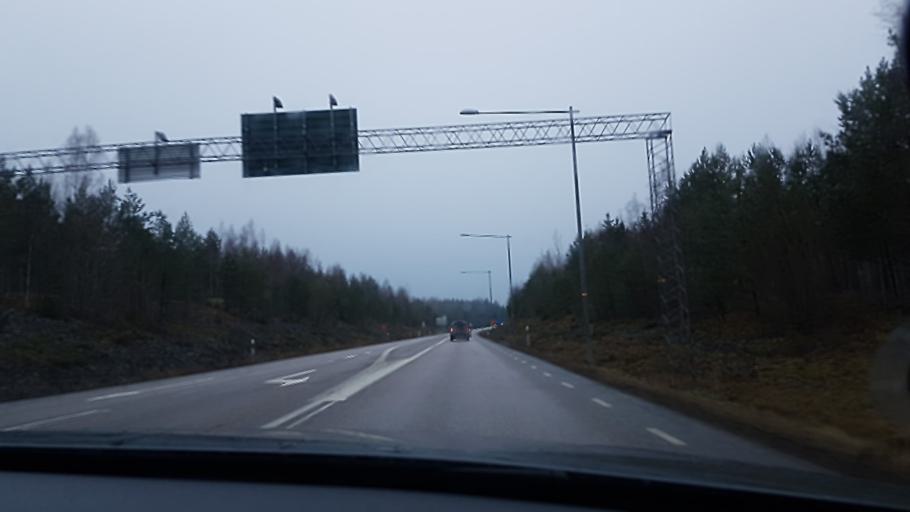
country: SE
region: Vaestra Goetaland
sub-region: Toreboda Kommun
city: Toereboda
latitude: 58.8298
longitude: 13.9890
